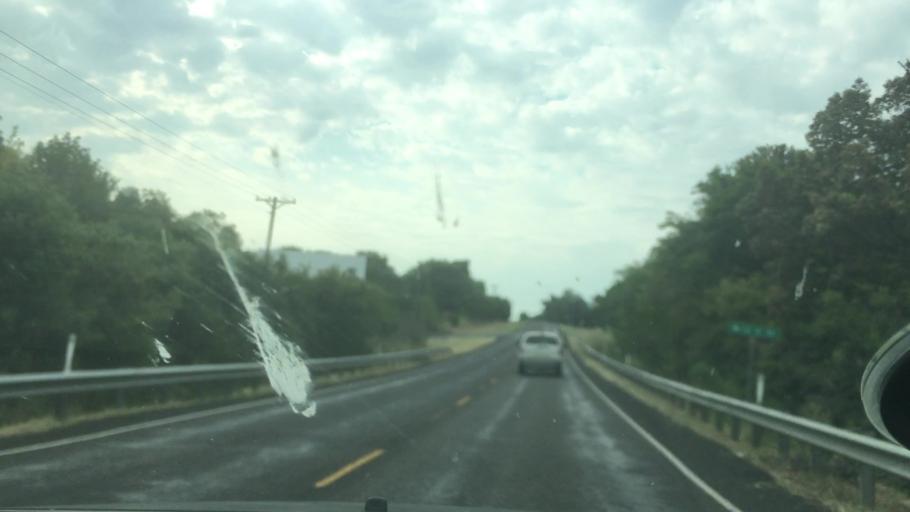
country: US
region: Texas
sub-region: Grayson County
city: Pottsboro
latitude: 33.7910
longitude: -96.6074
